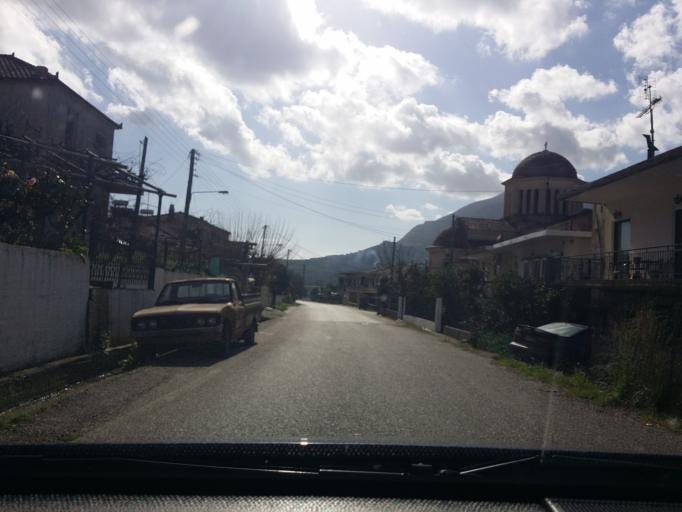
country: GR
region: West Greece
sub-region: Nomos Aitolias kai Akarnanias
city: Astakos
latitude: 38.5931
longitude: 21.0891
